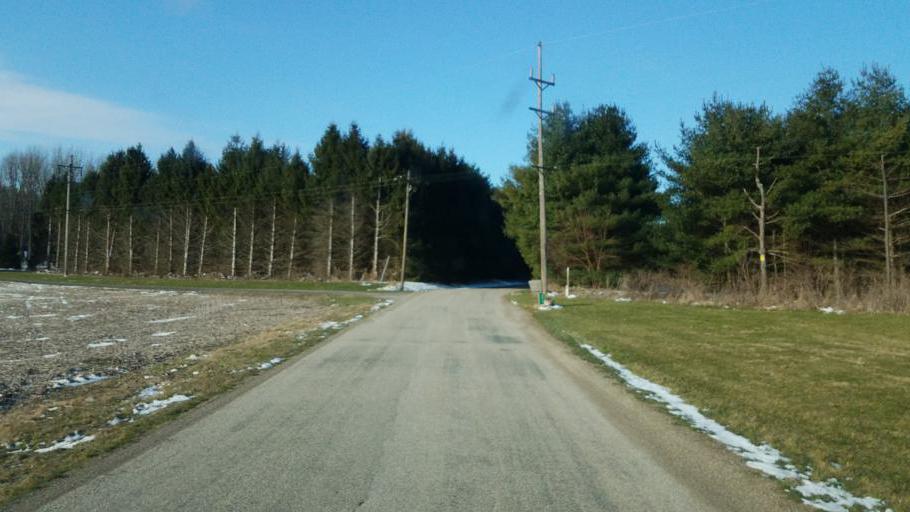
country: US
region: Ohio
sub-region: Sandusky County
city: Bellville
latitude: 40.6226
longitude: -82.5479
